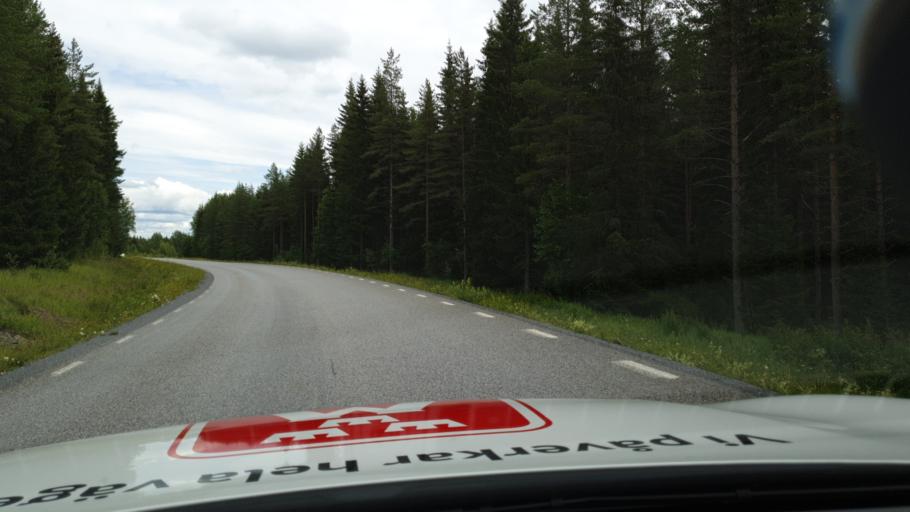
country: SE
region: Jaemtland
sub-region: OEstersunds Kommun
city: Lit
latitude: 63.3260
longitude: 14.8229
